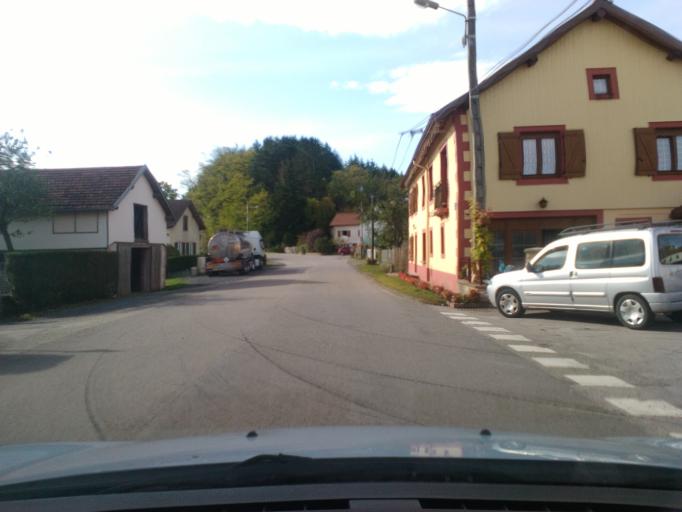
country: FR
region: Lorraine
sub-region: Departement des Vosges
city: Ban-de-Laveline
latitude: 48.2785
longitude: 7.0378
